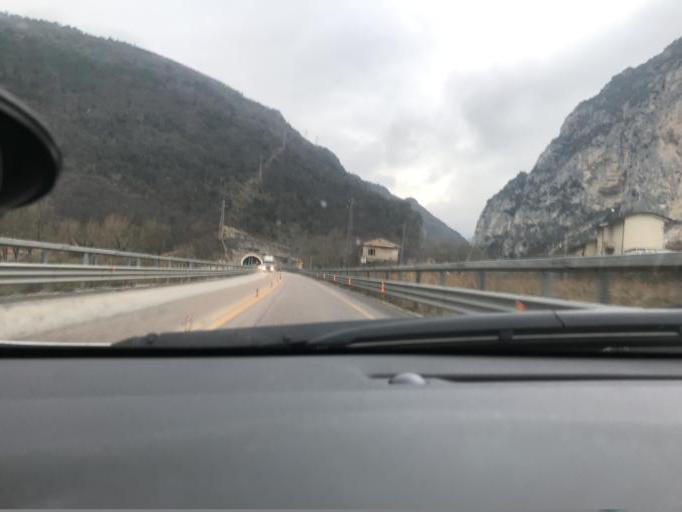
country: IT
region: The Marches
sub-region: Provincia di Ancona
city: Serra San Quirico
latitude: 43.4321
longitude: 13.0138
